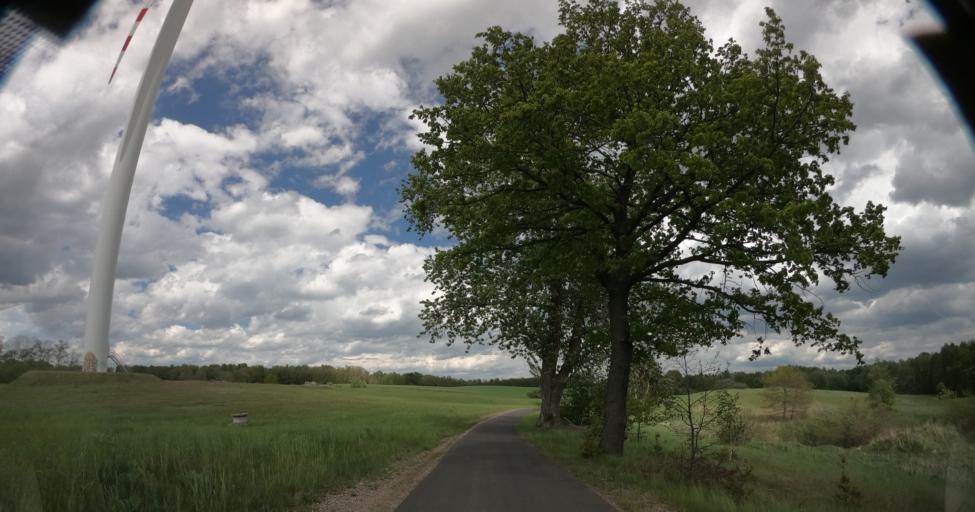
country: PL
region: West Pomeranian Voivodeship
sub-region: Powiat drawski
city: Drawsko Pomorskie
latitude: 53.5614
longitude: 15.7814
